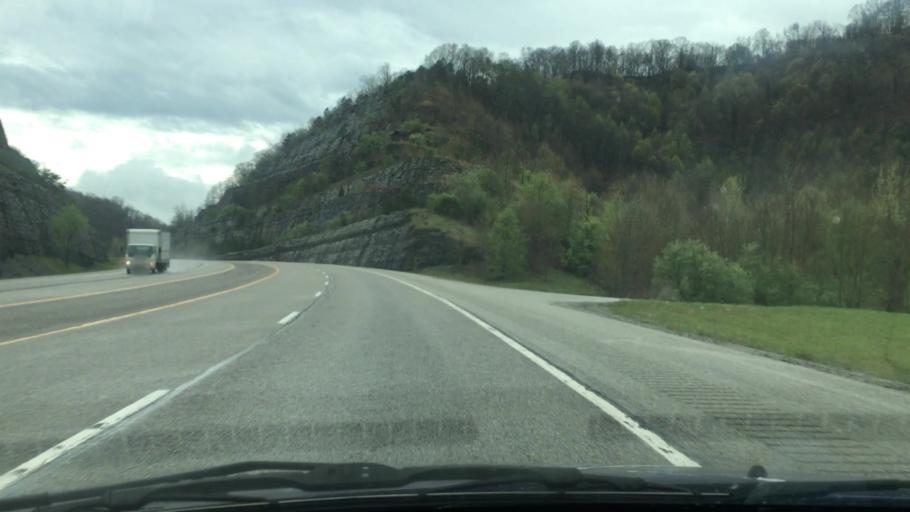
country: US
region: Kentucky
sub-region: Letcher County
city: Jenkins
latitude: 37.2174
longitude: -82.6276
